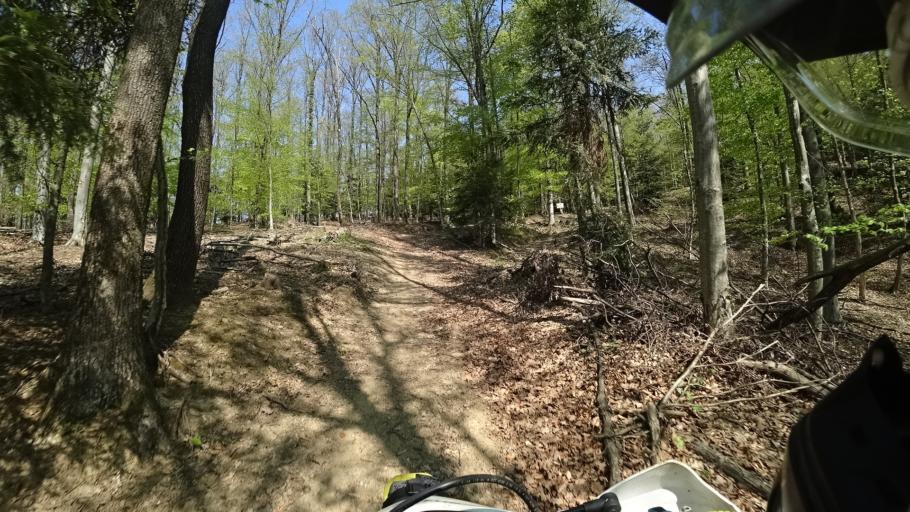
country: HR
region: Zagrebacka
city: Jakovlje
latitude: 45.9158
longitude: 15.9199
